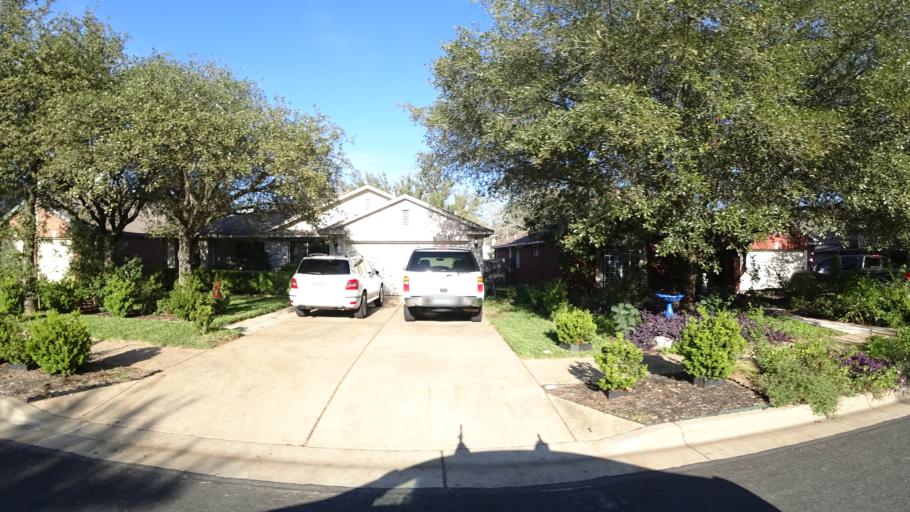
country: US
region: Texas
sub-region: Travis County
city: Shady Hollow
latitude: 30.2038
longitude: -97.8562
